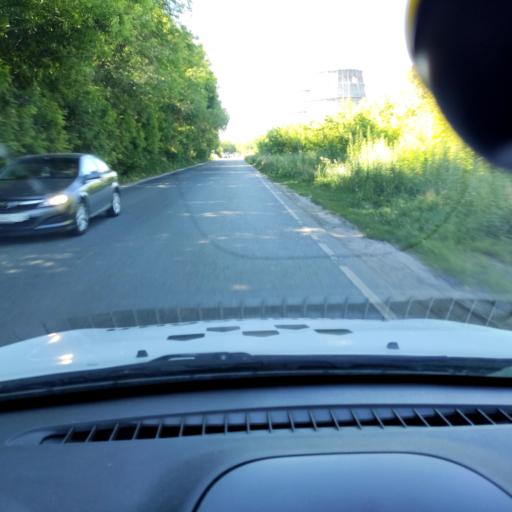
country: RU
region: Samara
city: Tol'yatti
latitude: 53.5803
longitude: 49.2560
